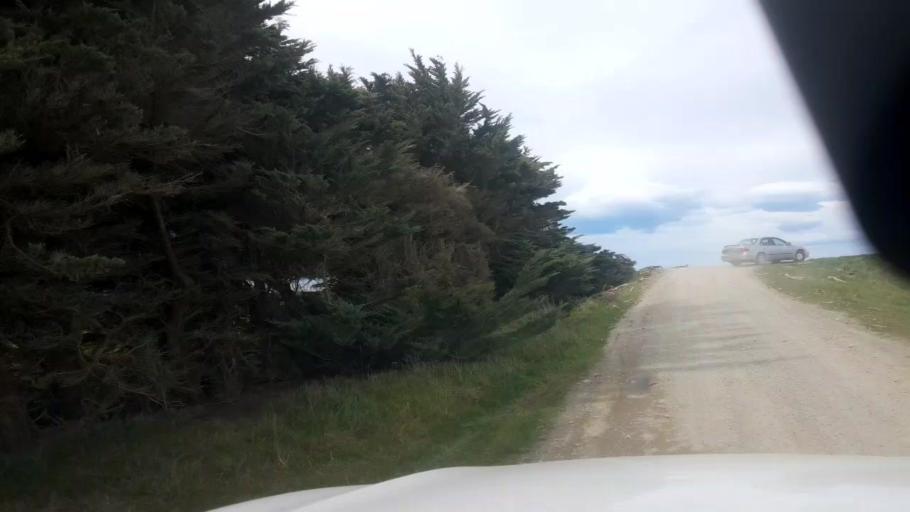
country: NZ
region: Canterbury
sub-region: Timaru District
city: Timaru
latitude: -44.2900
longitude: 171.3351
